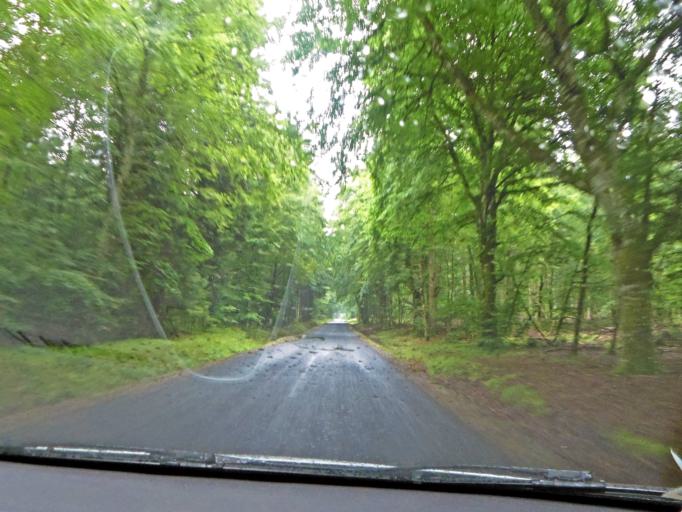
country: FR
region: Auvergne
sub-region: Departement du Puy-de-Dome
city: Orcines
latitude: 45.7446
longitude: 2.9402
